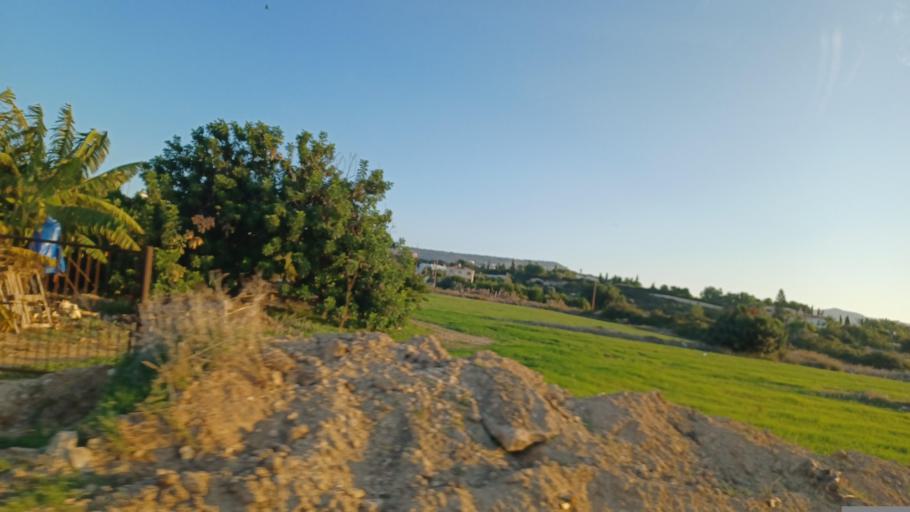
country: CY
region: Pafos
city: Pegeia
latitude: 34.8689
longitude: 32.3523
